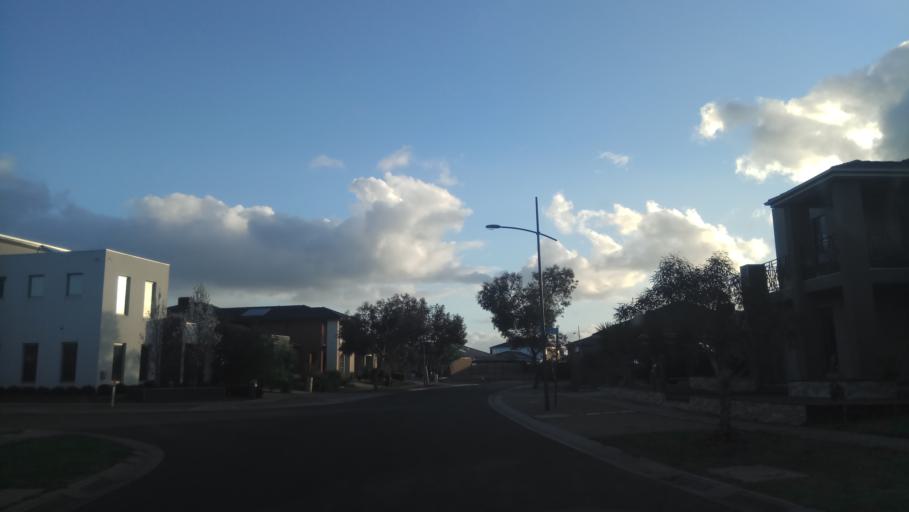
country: AU
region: Victoria
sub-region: Hobsons Bay
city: Altona Meadows
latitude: -37.9096
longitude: 144.7777
